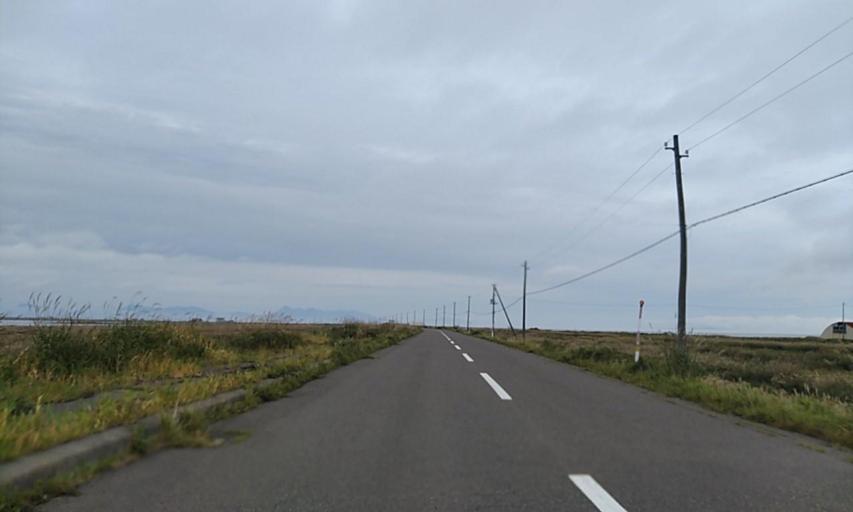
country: JP
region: Hokkaido
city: Shibetsu
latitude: 43.5761
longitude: 145.3435
